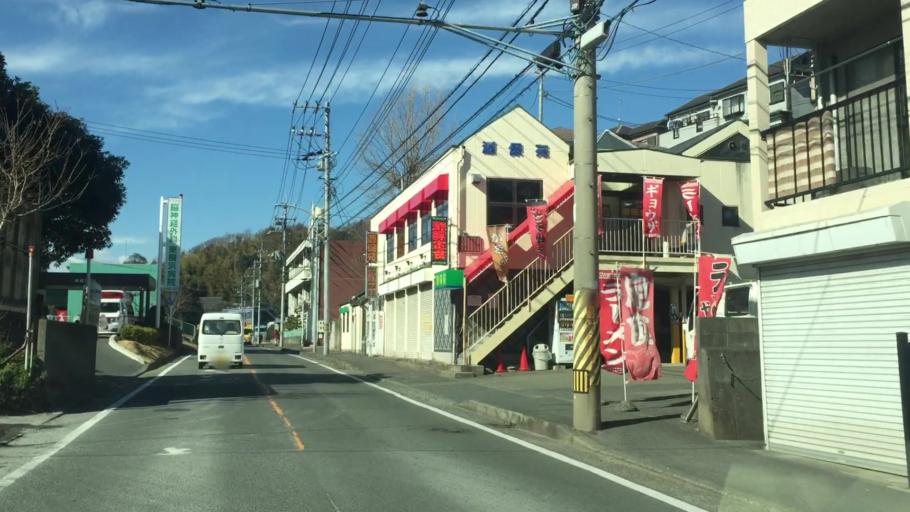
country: JP
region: Kanagawa
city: Yokohama
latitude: 35.4864
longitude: 139.5887
